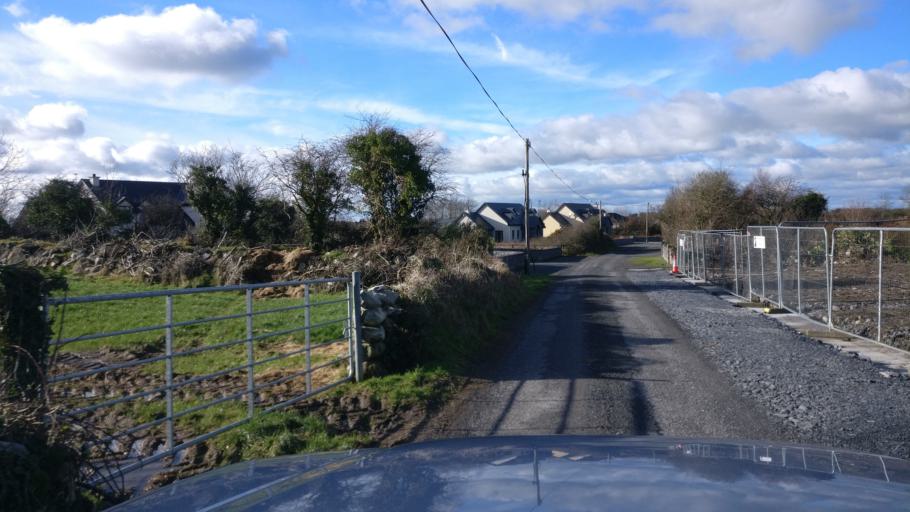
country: IE
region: Connaught
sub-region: County Galway
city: Athenry
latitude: 53.2250
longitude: -8.8085
